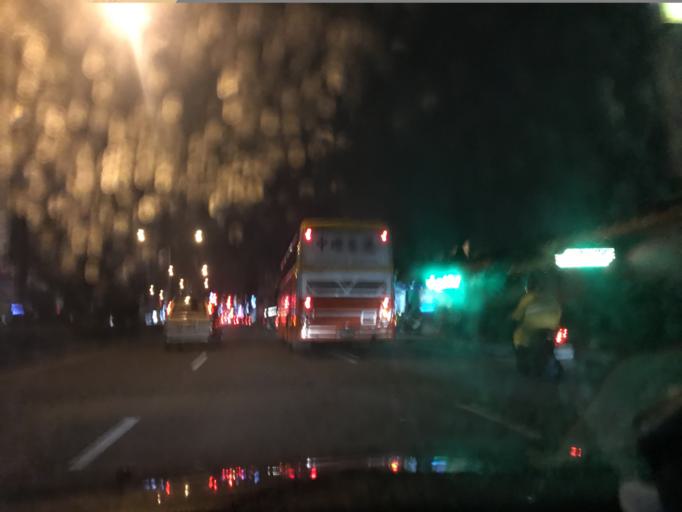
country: TW
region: Taiwan
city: Taoyuan City
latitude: 24.9493
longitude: 121.2427
